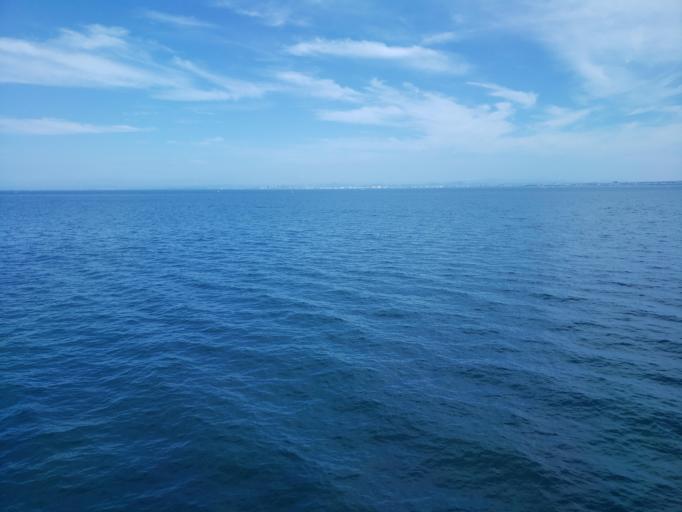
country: JP
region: Hyogo
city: Akashi
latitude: 34.5971
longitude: 134.9071
